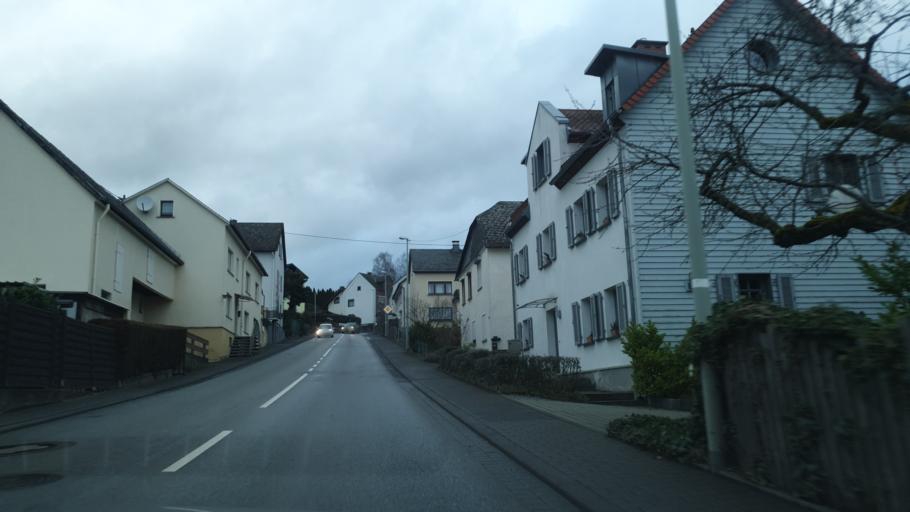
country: DE
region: Rheinland-Pfalz
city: Hirschberg
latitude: 50.3782
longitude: 7.9222
